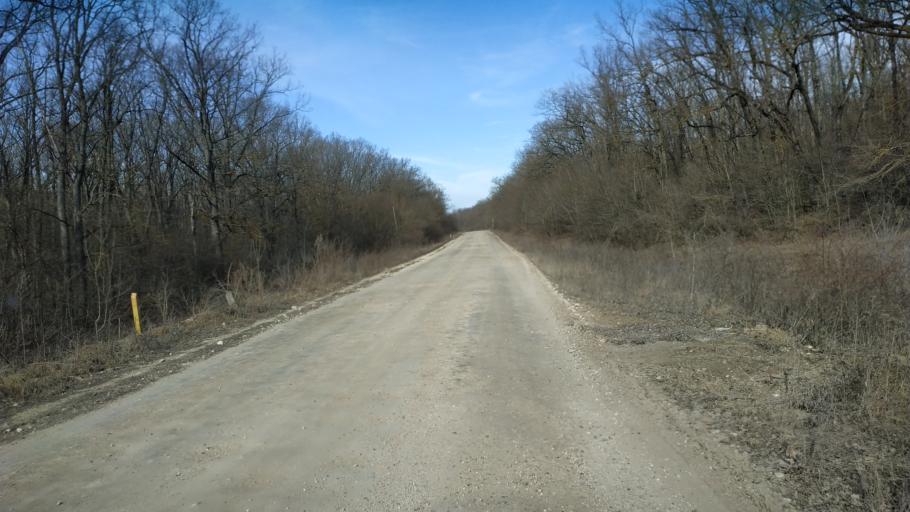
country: MD
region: Straseni
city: Straseni
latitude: 47.0359
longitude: 28.6151
